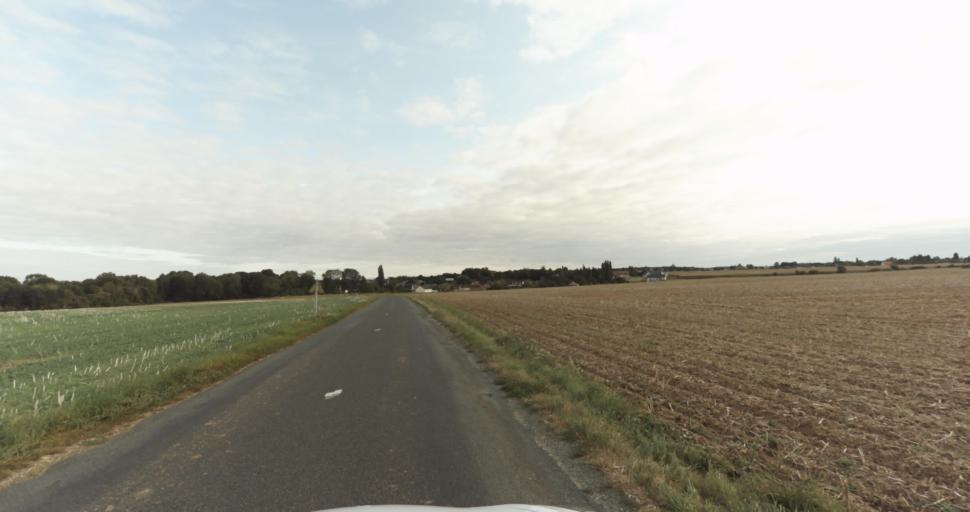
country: FR
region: Haute-Normandie
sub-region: Departement de l'Eure
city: Saint-Germain-sur-Avre
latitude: 48.8138
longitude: 1.2663
